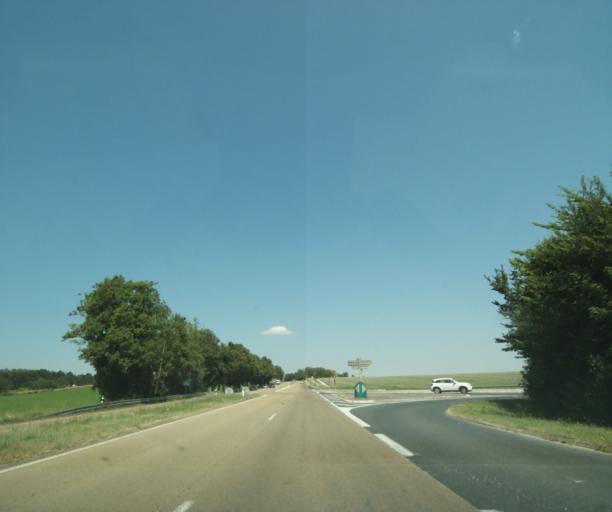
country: FR
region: Champagne-Ardenne
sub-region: Departement de la Marne
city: Verzy
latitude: 49.1142
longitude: 4.2534
